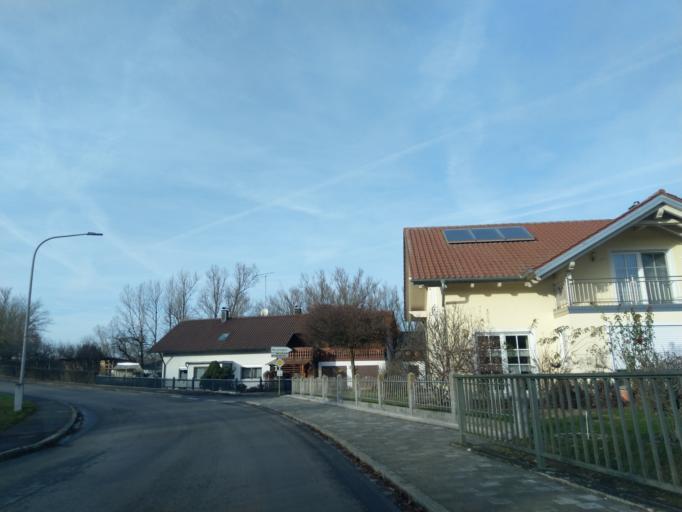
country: DE
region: Bavaria
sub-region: Lower Bavaria
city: Oberporing
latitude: 48.7042
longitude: 12.8230
